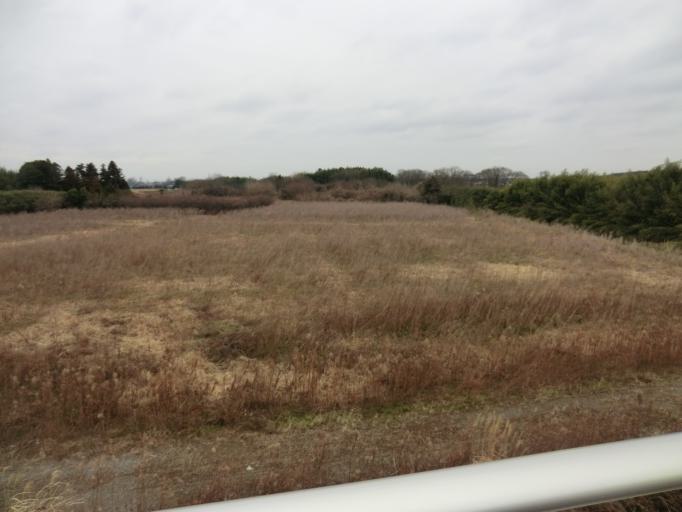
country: JP
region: Ibaraki
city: Naka
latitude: 36.1205
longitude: 140.1317
